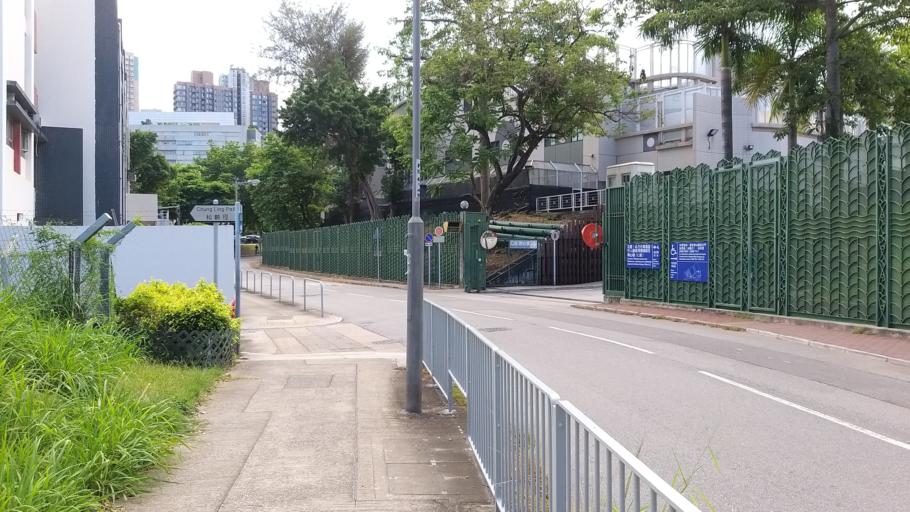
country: HK
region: Tuen Mun
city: Tuen Mun
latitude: 22.4087
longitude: 113.9726
